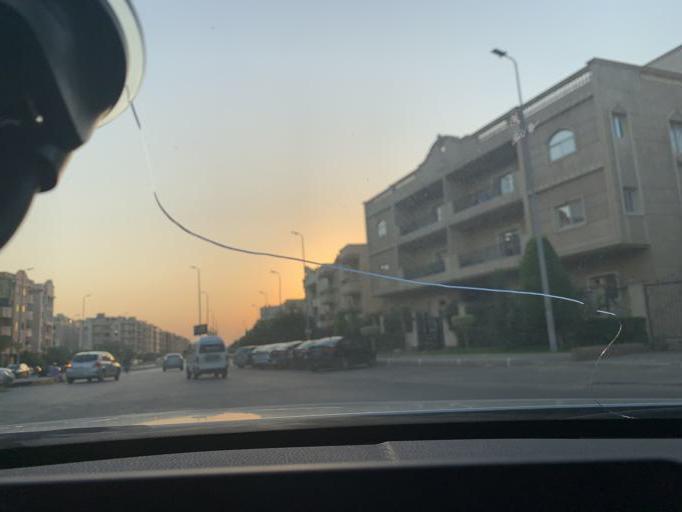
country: EG
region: Muhafazat al Qahirah
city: Cairo
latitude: 30.0060
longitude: 31.4546
